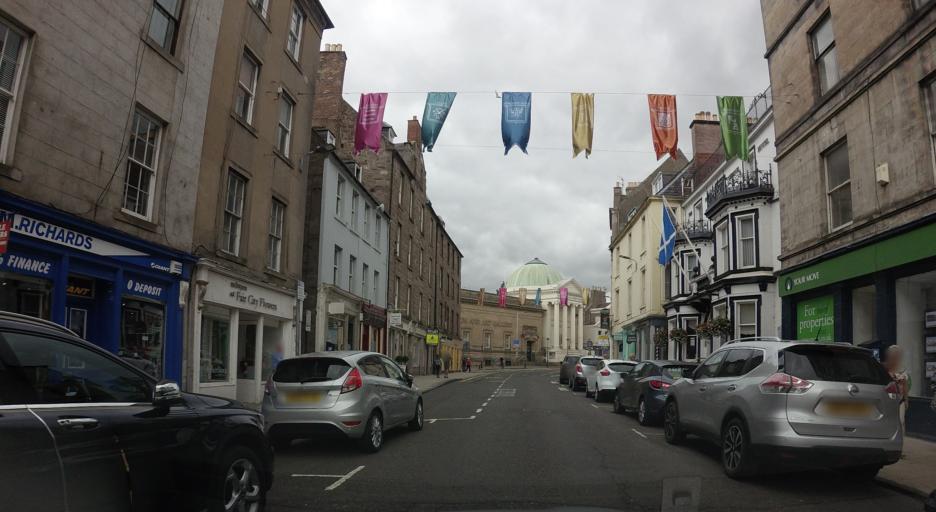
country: GB
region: Scotland
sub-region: Perth and Kinross
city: Perth
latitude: 56.3976
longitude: -3.4276
